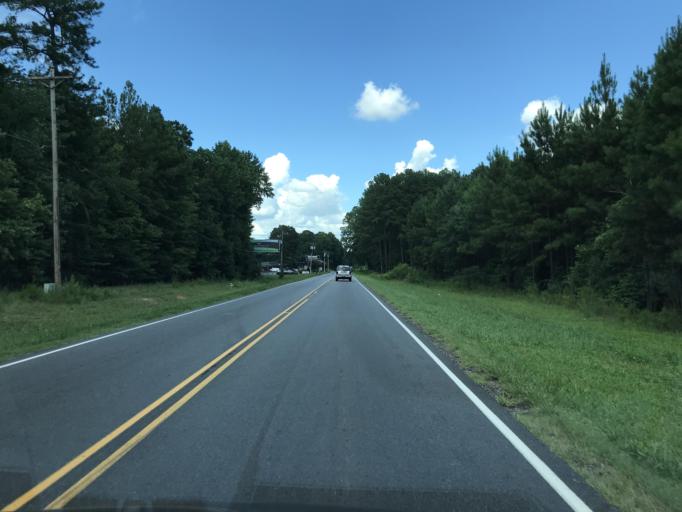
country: US
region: North Carolina
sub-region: Catawba County
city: Lake Norman of Catawba
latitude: 35.5979
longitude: -80.9582
